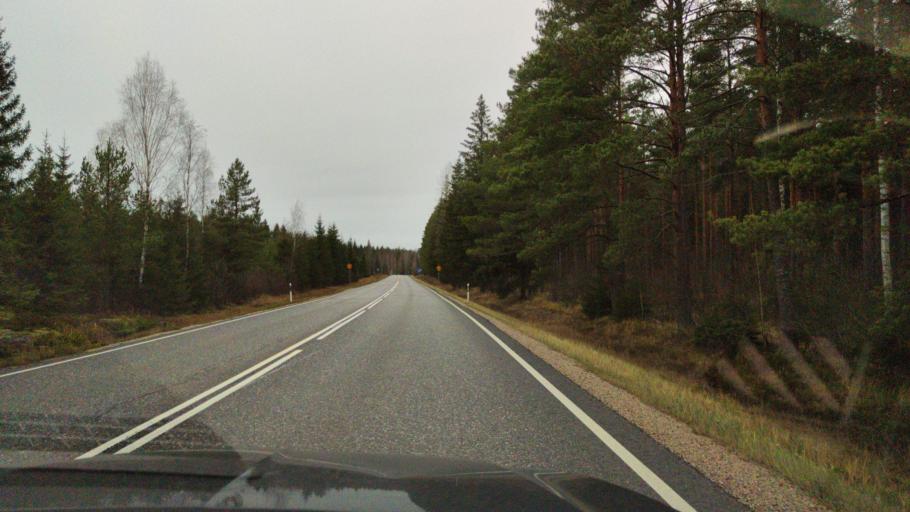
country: FI
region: Varsinais-Suomi
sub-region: Loimaa
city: Ylaene
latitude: 60.7360
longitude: 22.4321
